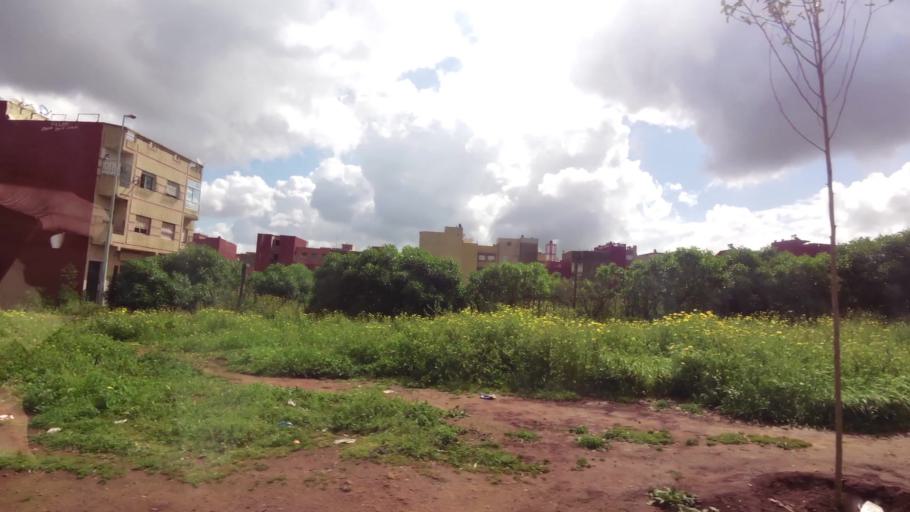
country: MA
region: Grand Casablanca
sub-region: Nouaceur
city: Bouskoura
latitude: 33.5090
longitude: -7.6507
